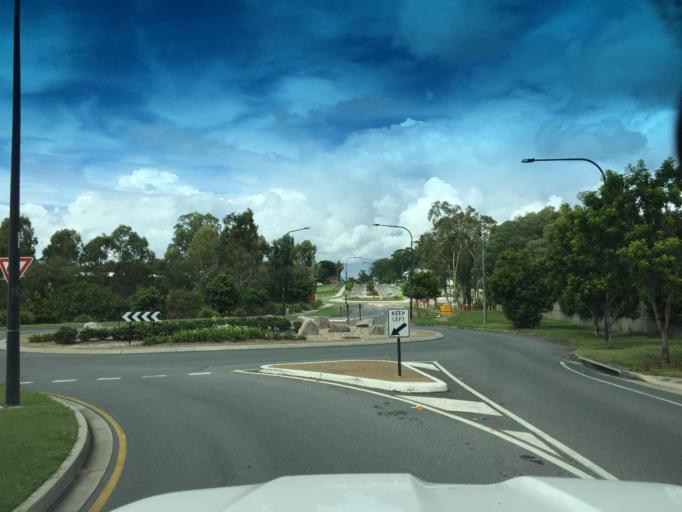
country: AU
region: Queensland
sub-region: Moreton Bay
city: Mango Hill
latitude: -27.2257
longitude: 153.0295
